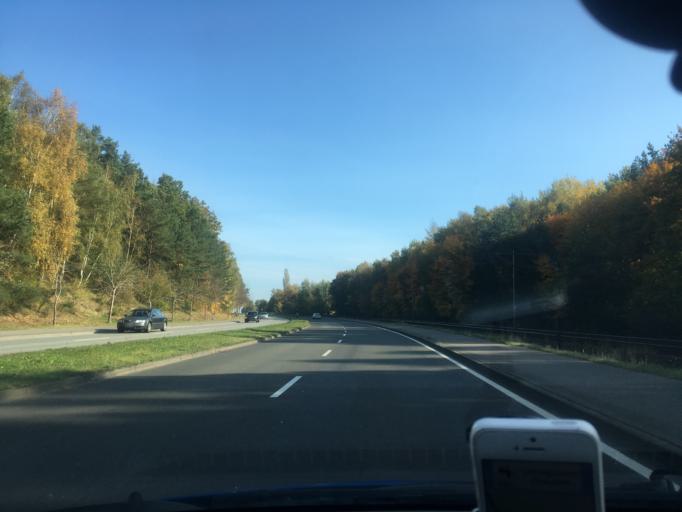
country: DE
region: Mecklenburg-Vorpommern
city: Feldstadt
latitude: 53.5941
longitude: 11.4182
